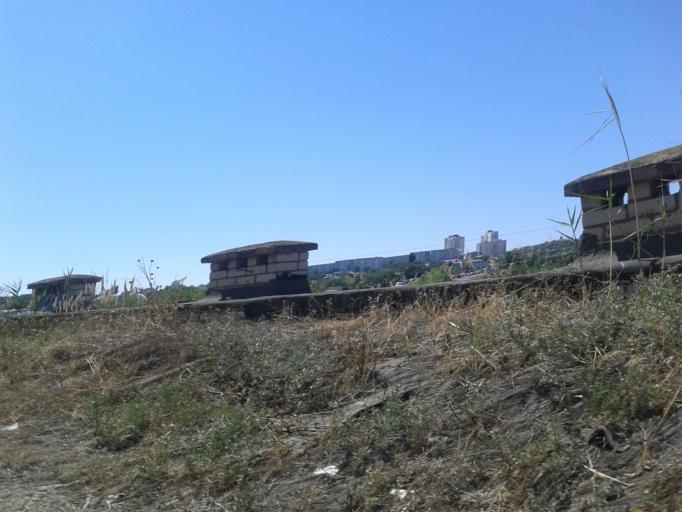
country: RU
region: Volgograd
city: Volgograd
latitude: 48.6880
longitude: 44.4529
